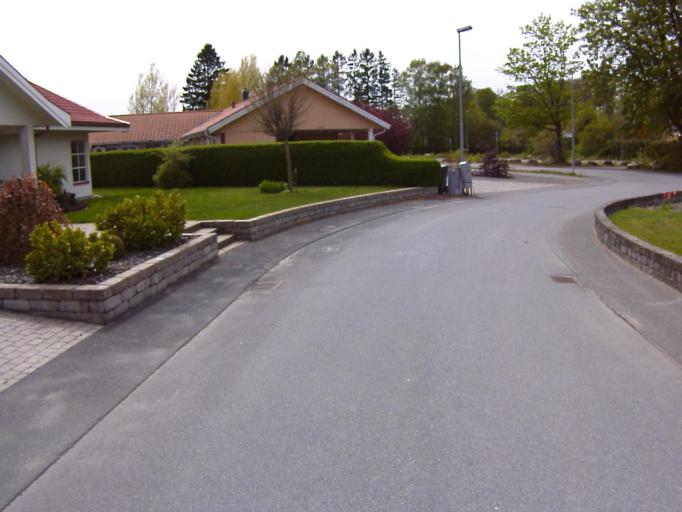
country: SE
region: Skane
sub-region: Kristianstads Kommun
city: Fjalkinge
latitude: 56.0783
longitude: 14.2160
